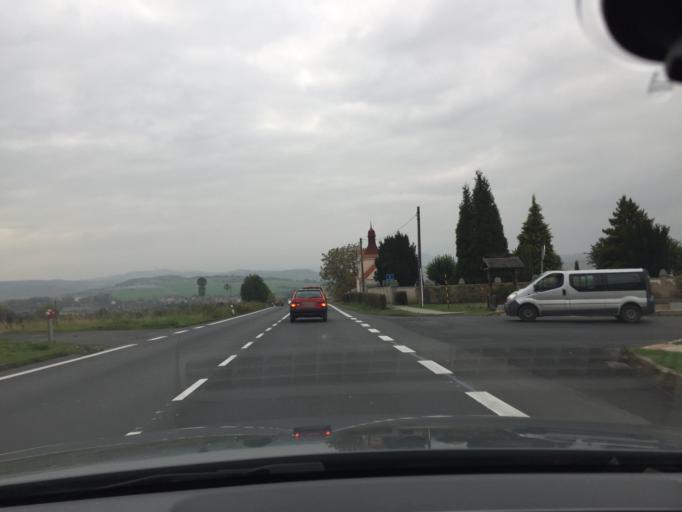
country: CZ
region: Ustecky
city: Rehlovice
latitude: 50.5821
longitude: 13.9252
